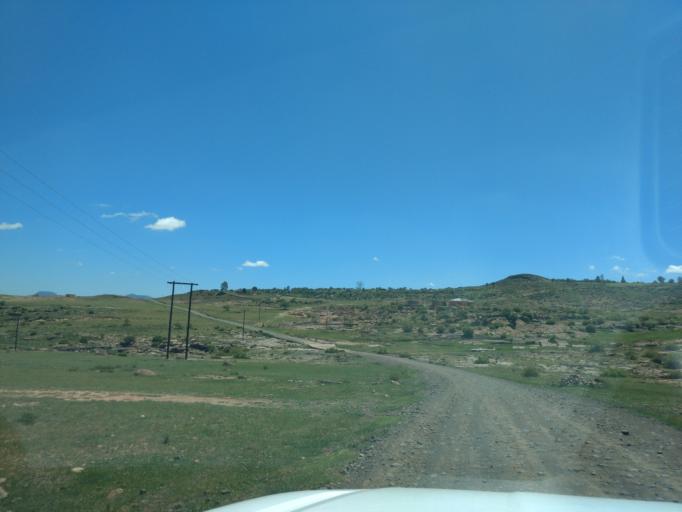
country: LS
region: Maseru
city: Maseru
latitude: -29.4668
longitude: 27.3759
